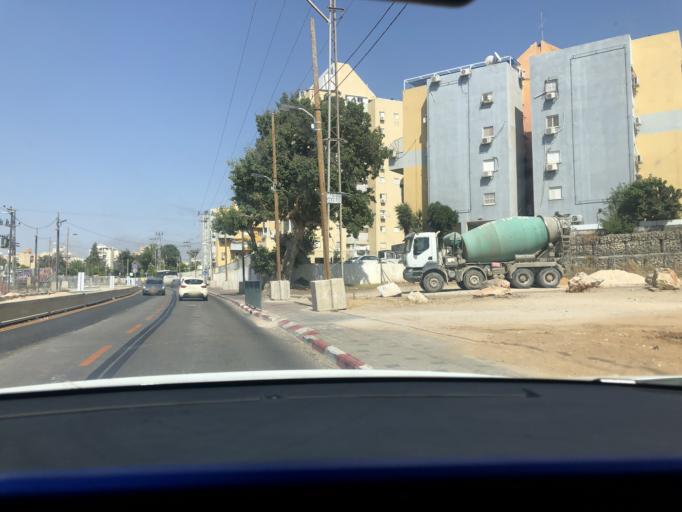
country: IL
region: Central District
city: Lod
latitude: 31.9441
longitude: 34.8753
